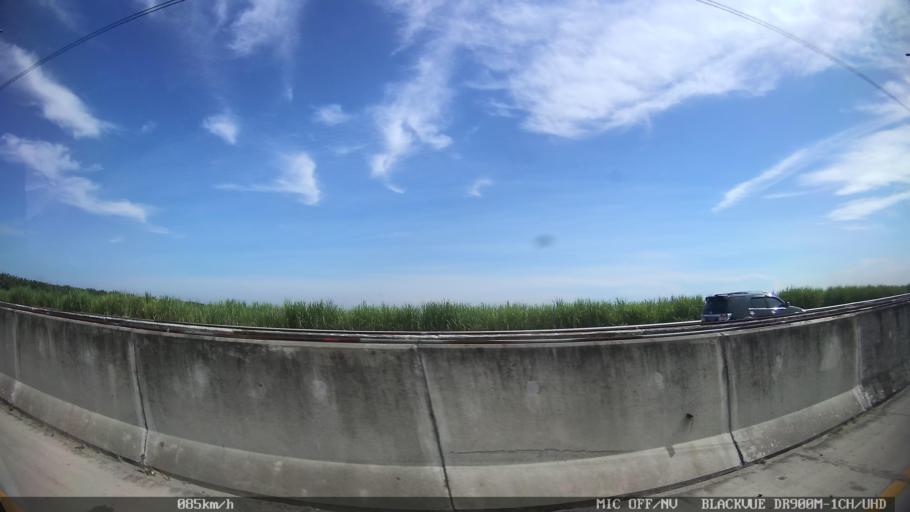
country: ID
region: North Sumatra
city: Sunggal
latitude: 3.6384
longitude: 98.6194
